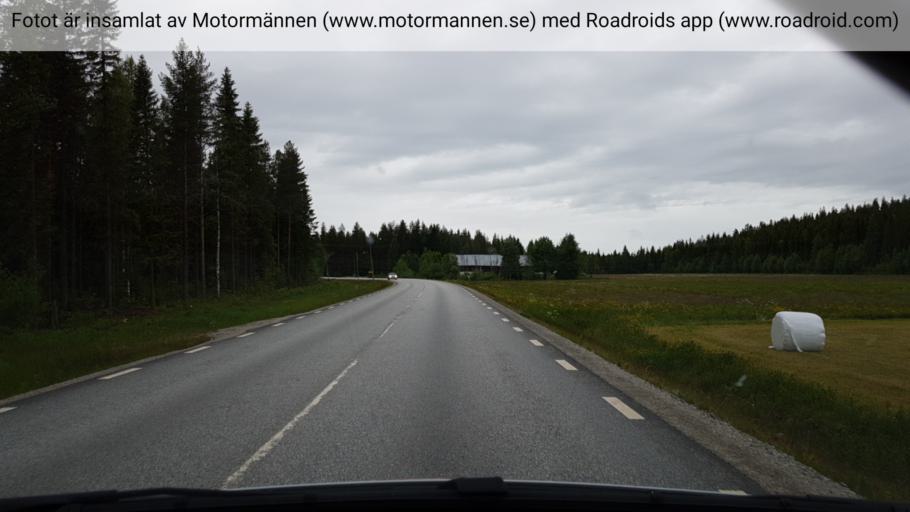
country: SE
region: Vaesterbotten
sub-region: Vindelns Kommun
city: Vindeln
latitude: 64.1999
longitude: 19.4500
